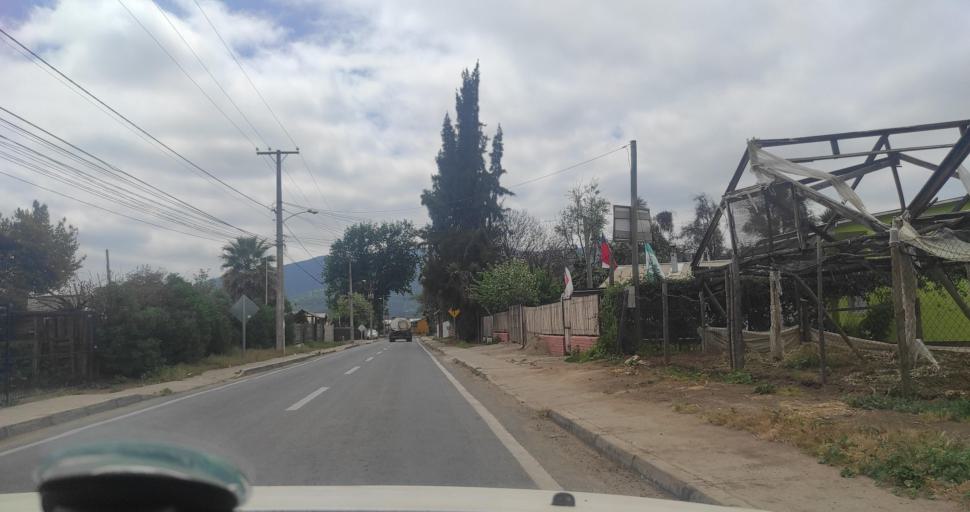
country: CL
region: Valparaiso
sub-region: Provincia de Marga Marga
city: Limache
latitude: -33.0156
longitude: -71.2429
